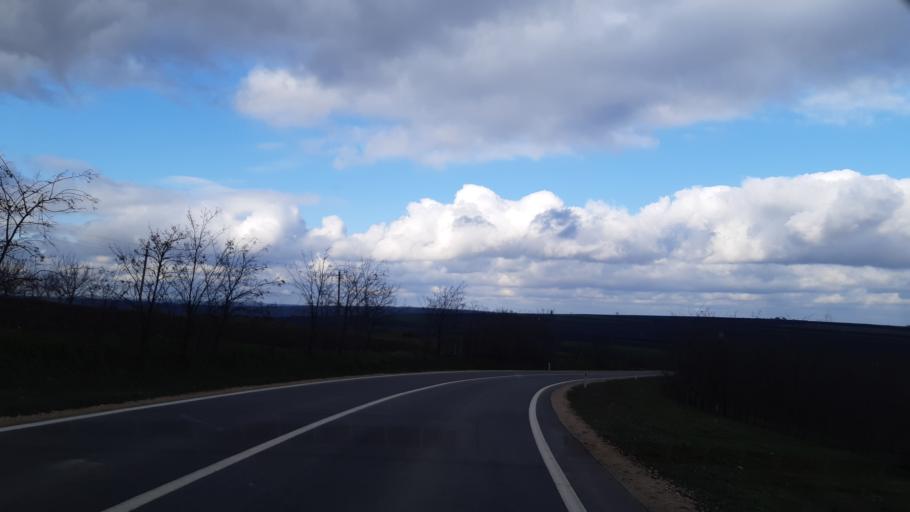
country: MD
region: Chisinau
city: Ciorescu
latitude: 47.2338
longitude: 28.9714
